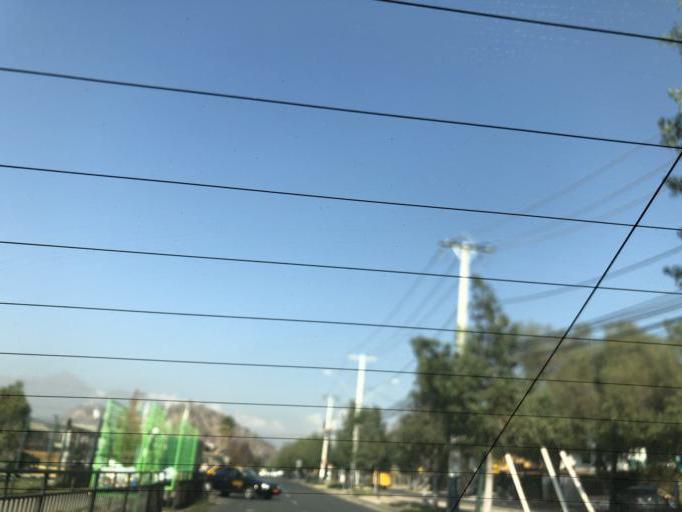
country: CL
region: Santiago Metropolitan
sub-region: Provincia de Cordillera
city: Puente Alto
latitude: -33.5943
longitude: -70.5591
